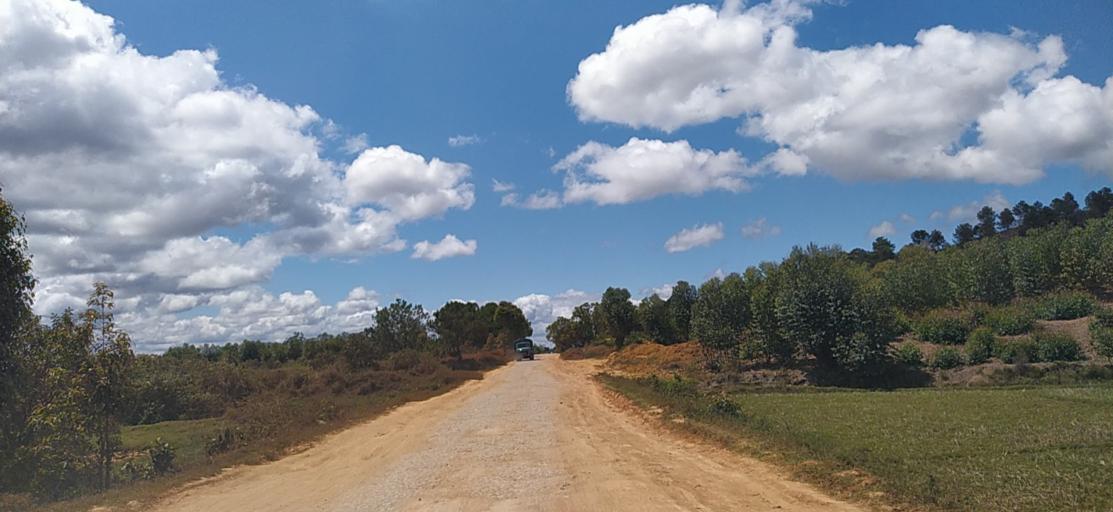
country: MG
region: Alaotra Mangoro
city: Moramanga
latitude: -18.7059
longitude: 48.2712
